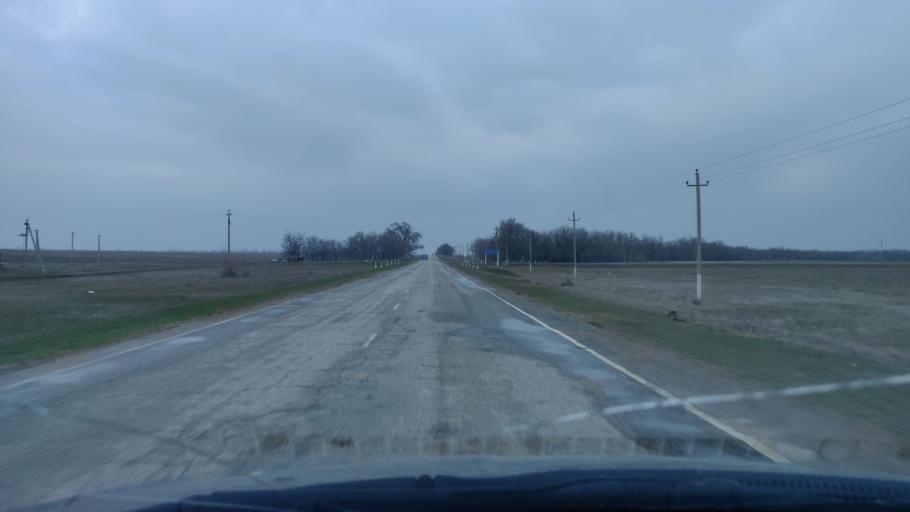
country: RU
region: Stavropol'skiy
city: Letnyaya Stavka
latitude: 45.3792
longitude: 43.3274
